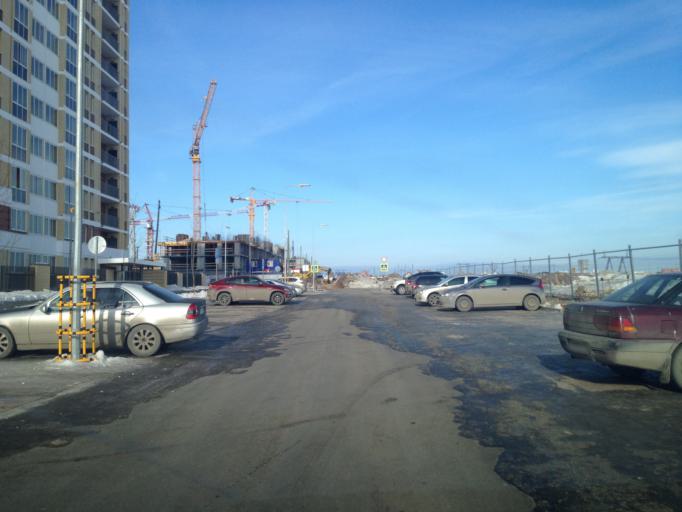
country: RU
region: Sverdlovsk
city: Sovkhoznyy
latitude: 56.7470
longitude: 60.5686
